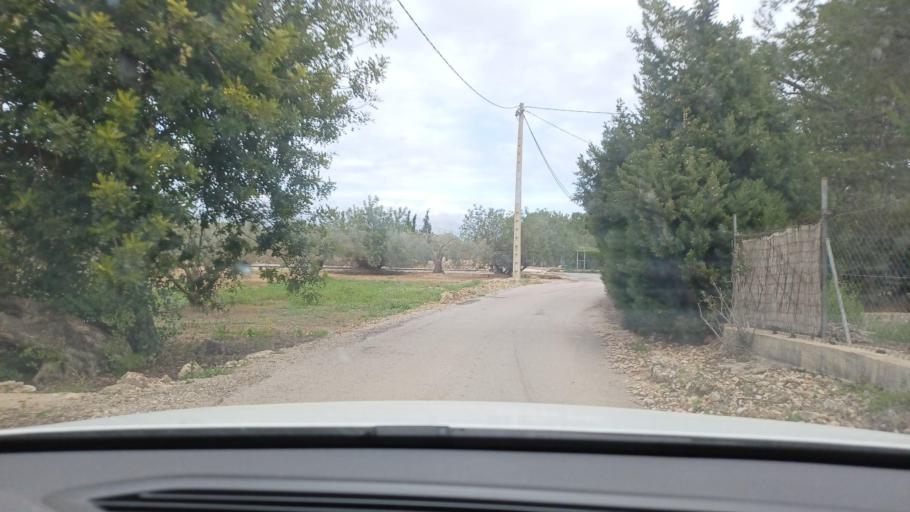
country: ES
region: Catalonia
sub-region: Provincia de Tarragona
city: Tortosa
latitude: 40.7936
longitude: 0.4620
